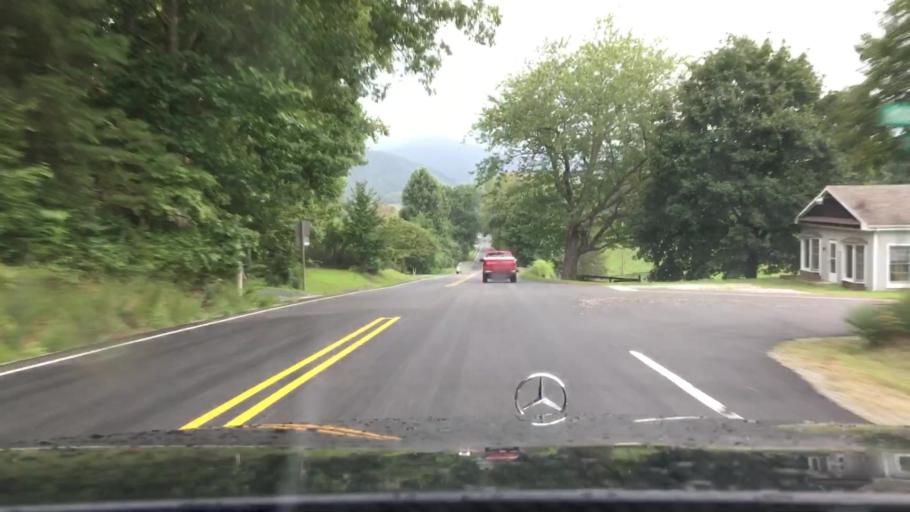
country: US
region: Virginia
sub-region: Nelson County
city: Nellysford
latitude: 37.9066
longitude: -78.8523
